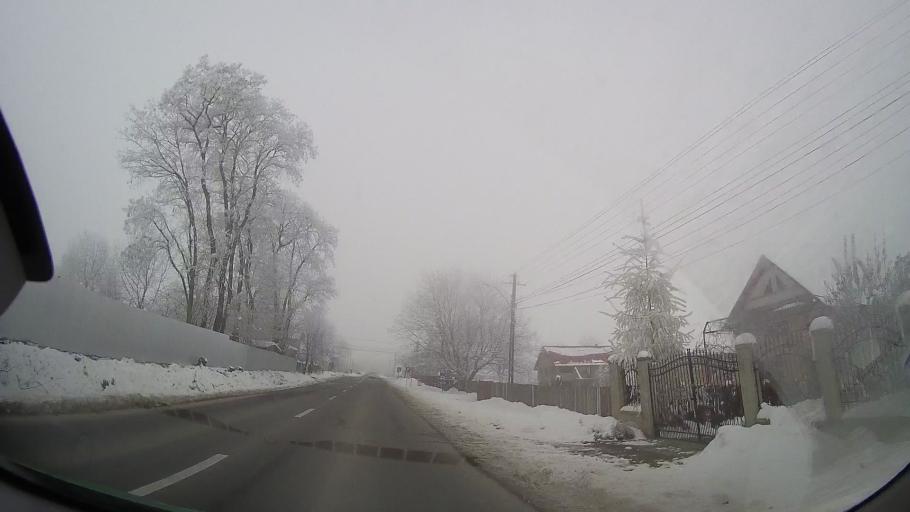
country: RO
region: Iasi
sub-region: Comuna Valea Seaca
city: Valea Seaca
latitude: 47.2939
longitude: 26.6739
